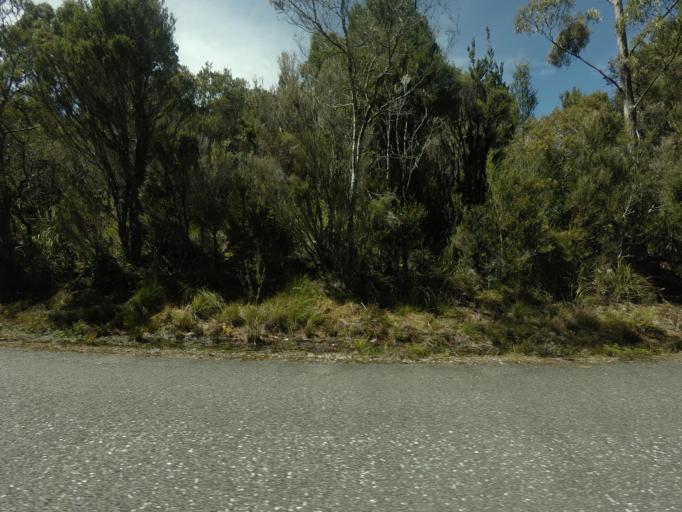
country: AU
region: Tasmania
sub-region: West Coast
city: Queenstown
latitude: -42.7742
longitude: 146.0574
